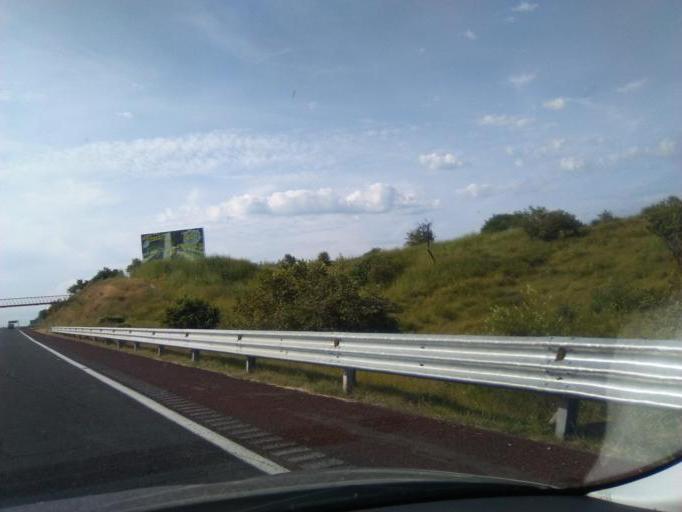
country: MX
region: Morelos
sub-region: Jojutla
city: Tehuixtla
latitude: 18.5859
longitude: -99.2549
